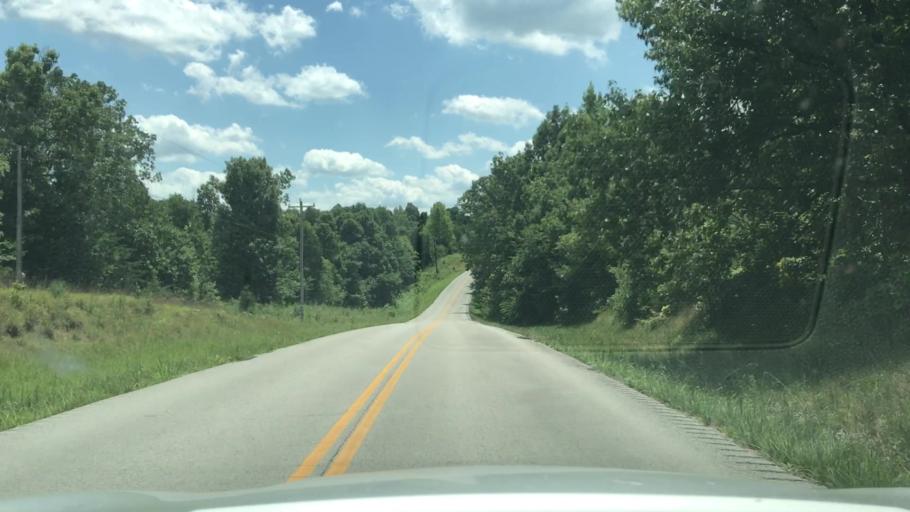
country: US
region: Kentucky
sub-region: Hopkins County
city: Nortonville
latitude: 37.1089
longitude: -87.3343
